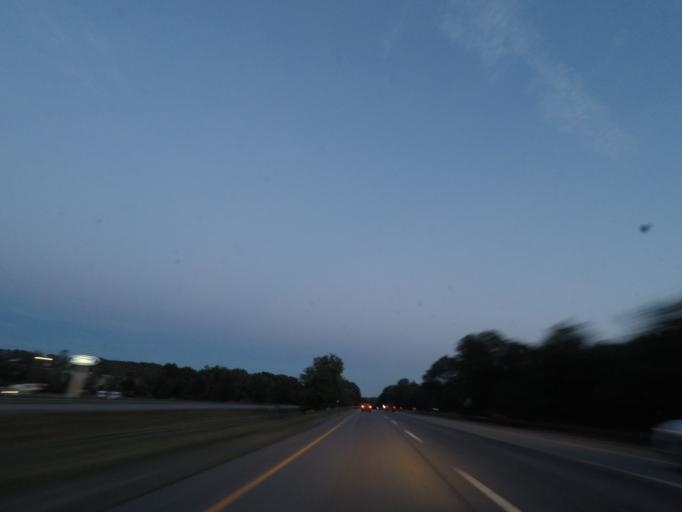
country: US
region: Connecticut
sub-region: Windham County
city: Putnam
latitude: 41.8972
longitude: -71.8985
